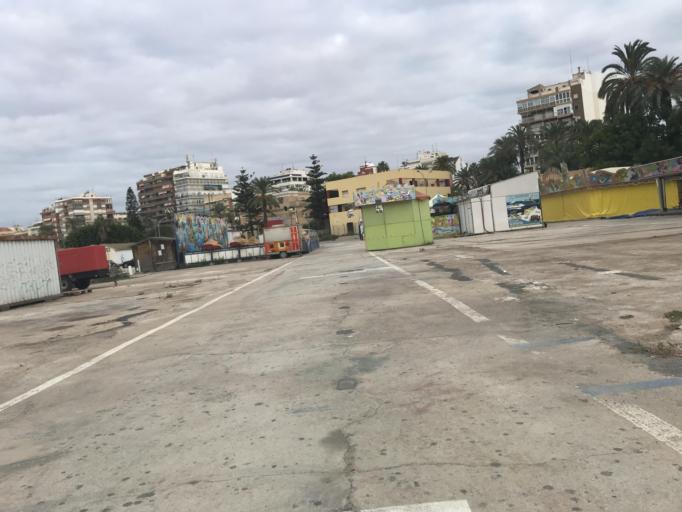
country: ES
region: Valencia
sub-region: Provincia de Alicante
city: Torrevieja
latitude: 37.9745
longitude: -0.6794
